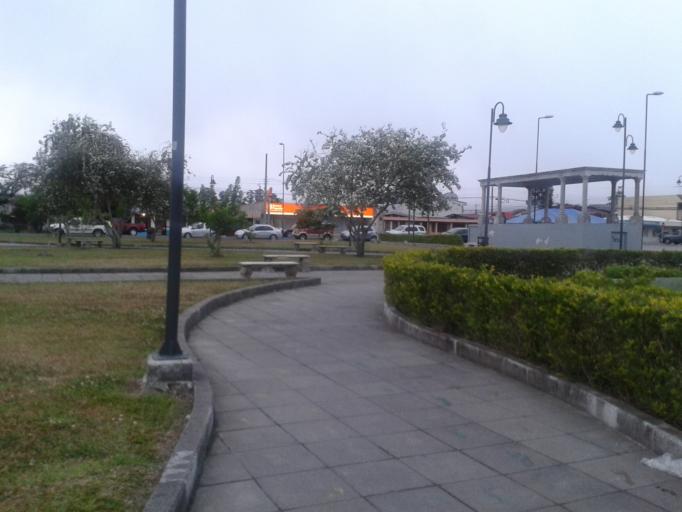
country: CR
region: Cartago
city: Cartago
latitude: 9.8444
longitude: -83.9386
